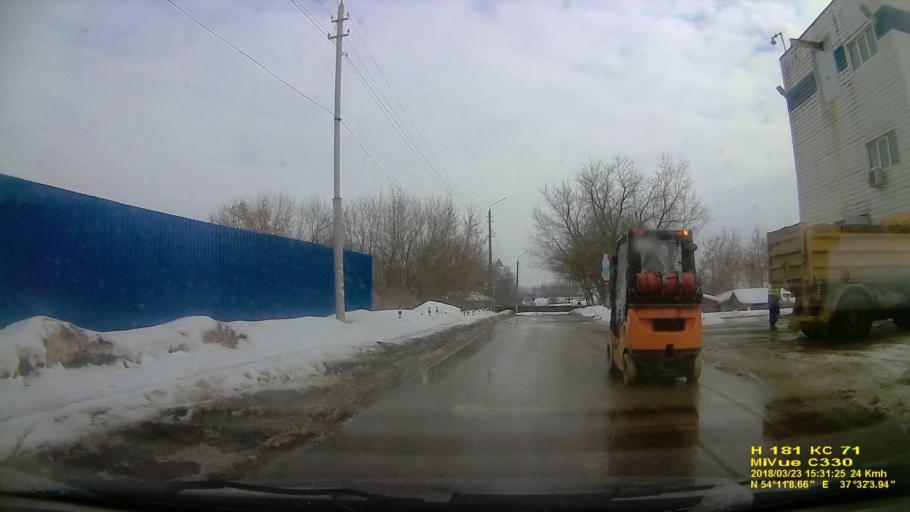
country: RU
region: Tula
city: Kosaya Gora
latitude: 54.1857
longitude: 37.5345
